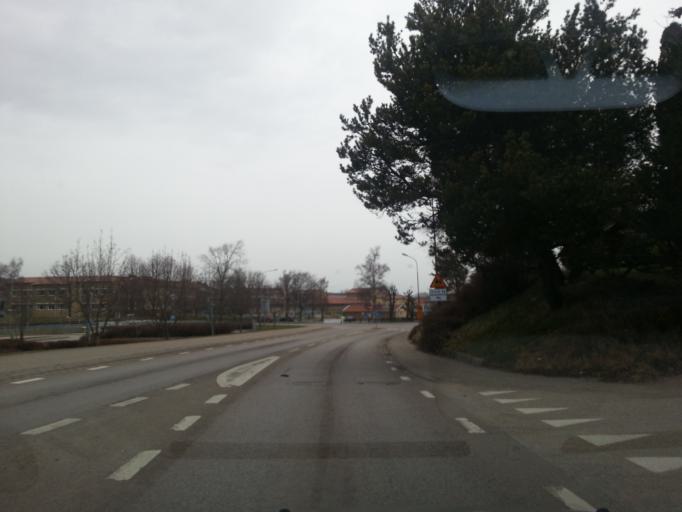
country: SE
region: Vaestra Goetaland
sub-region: Lilla Edets Kommun
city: Lilla Edet
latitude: 58.1324
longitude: 12.1260
